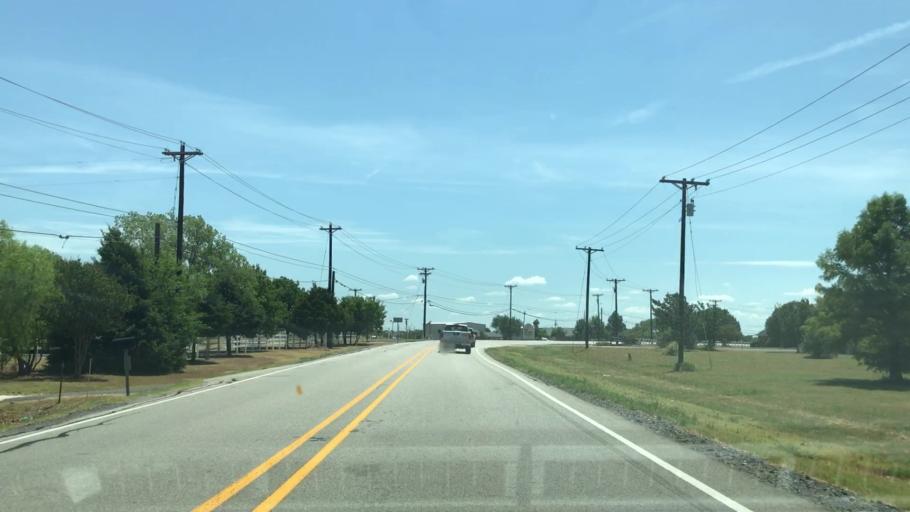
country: US
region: Texas
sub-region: Collin County
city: Saint Paul
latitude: 33.0345
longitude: -96.5490
